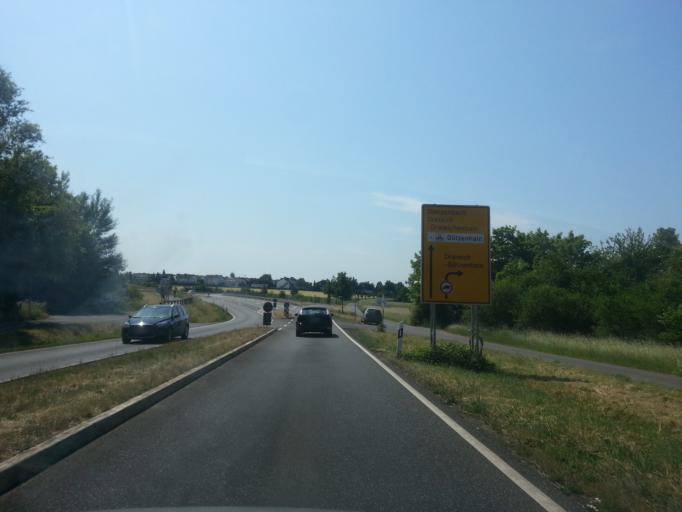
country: DE
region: Hesse
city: Dreieich
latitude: 50.0088
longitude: 8.7307
